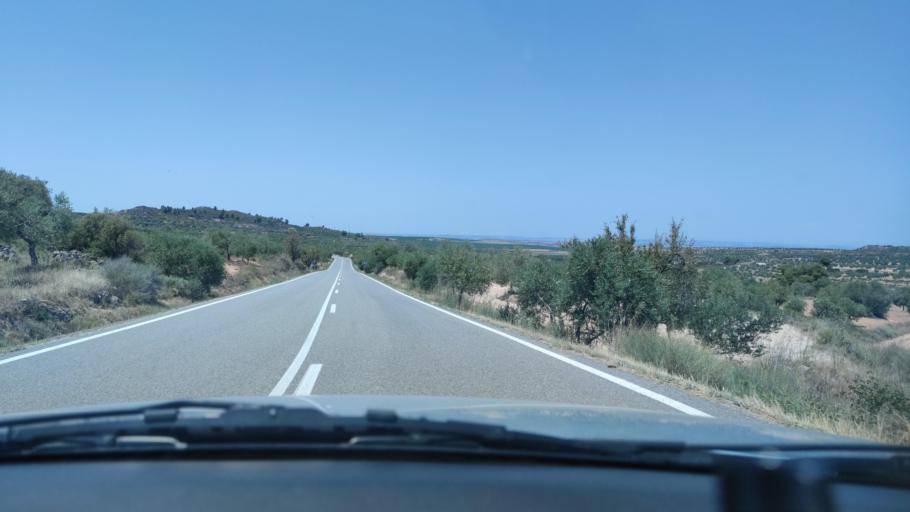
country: ES
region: Catalonia
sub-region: Provincia de Lleida
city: el Cogul
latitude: 41.4428
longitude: 0.6454
